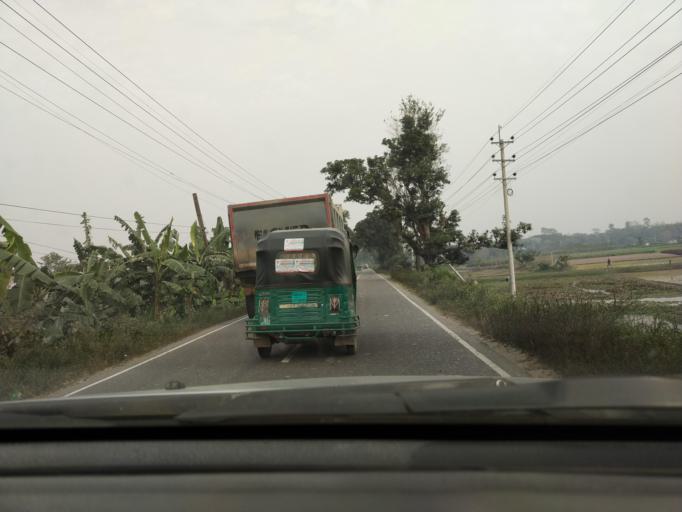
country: BD
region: Dhaka
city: Narsingdi
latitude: 24.0180
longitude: 90.7375
